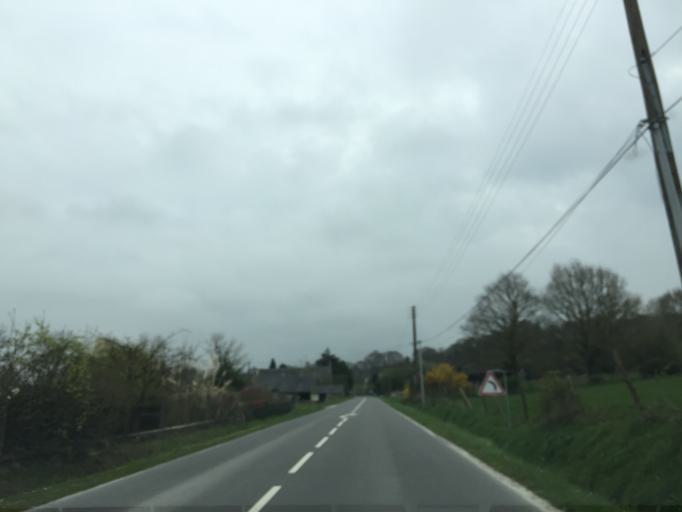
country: FR
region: Brittany
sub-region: Departement d'Ille-et-Vilaine
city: Roz-sur-Couesnon
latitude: 48.5859
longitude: -1.5786
